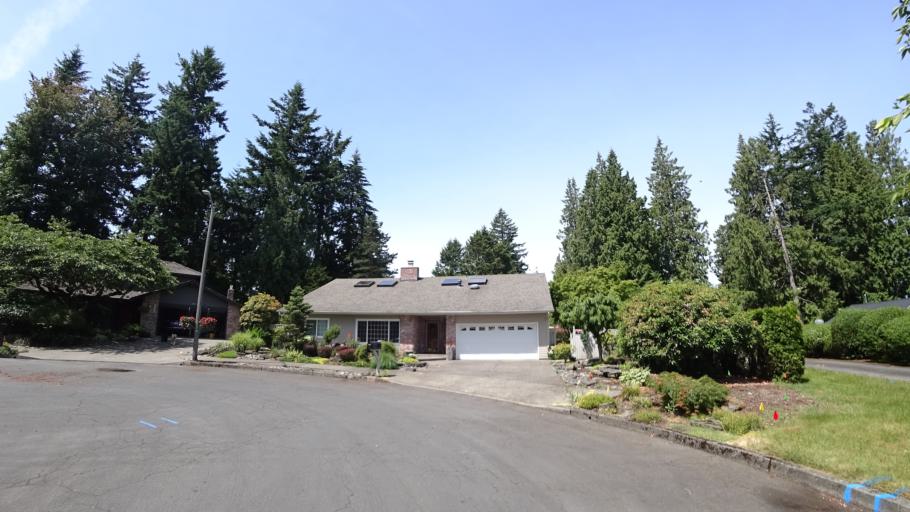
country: US
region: Oregon
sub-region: Multnomah County
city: Fairview
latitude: 45.5448
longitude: -122.5005
